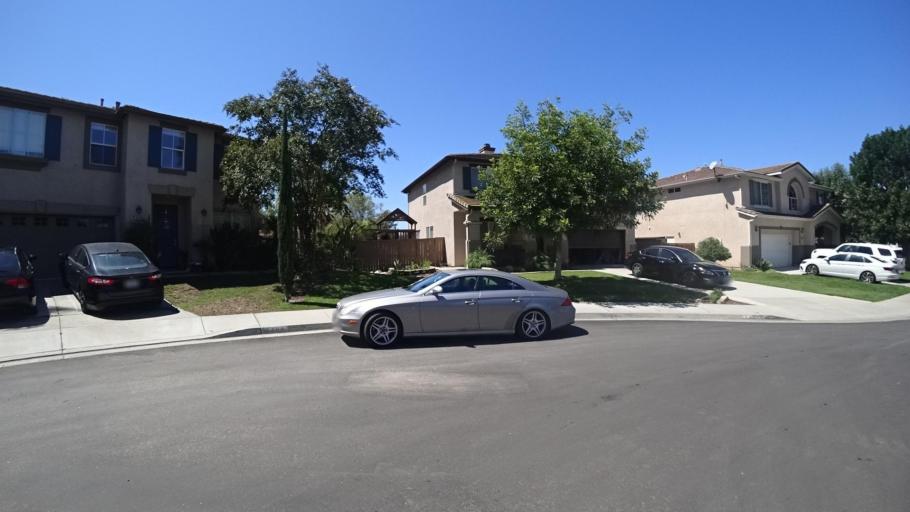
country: US
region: California
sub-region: San Diego County
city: Rainbow
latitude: 33.3261
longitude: -117.1474
